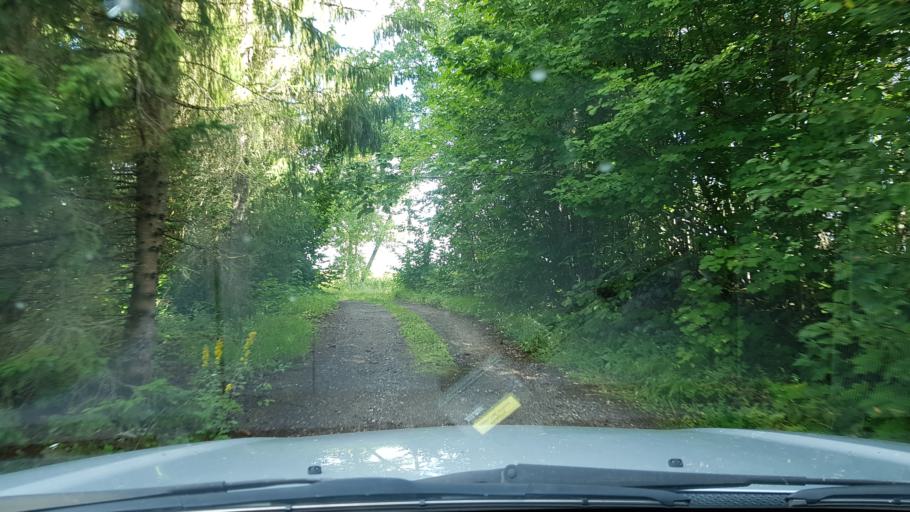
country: EE
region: Harju
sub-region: Rae vald
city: Vaida
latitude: 59.2676
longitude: 25.0283
